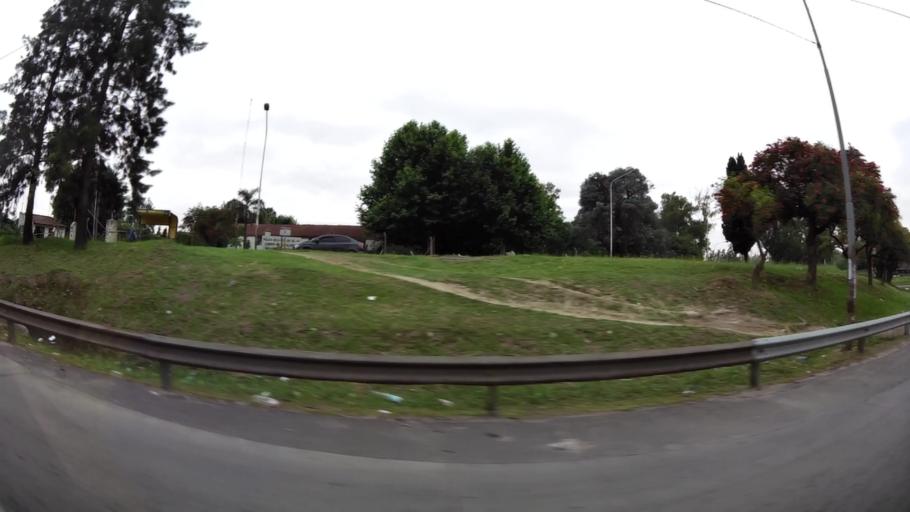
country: AR
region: Buenos Aires F.D.
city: Villa Lugano
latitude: -34.7207
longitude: -58.5143
